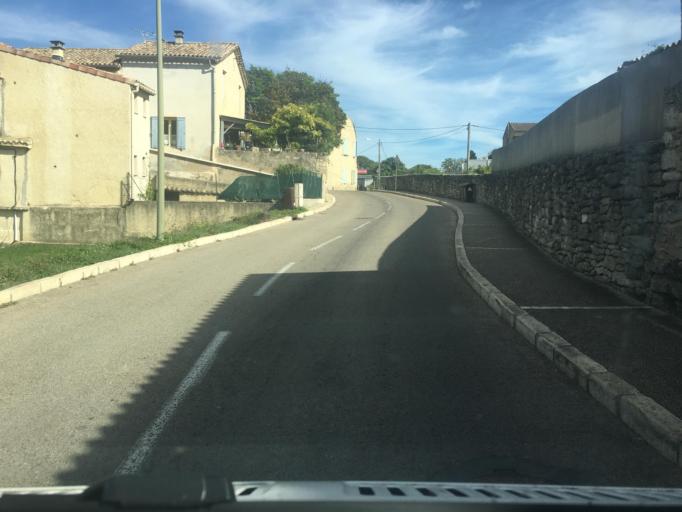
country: FR
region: Languedoc-Roussillon
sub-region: Departement du Gard
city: Uzes
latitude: 44.0172
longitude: 4.4207
